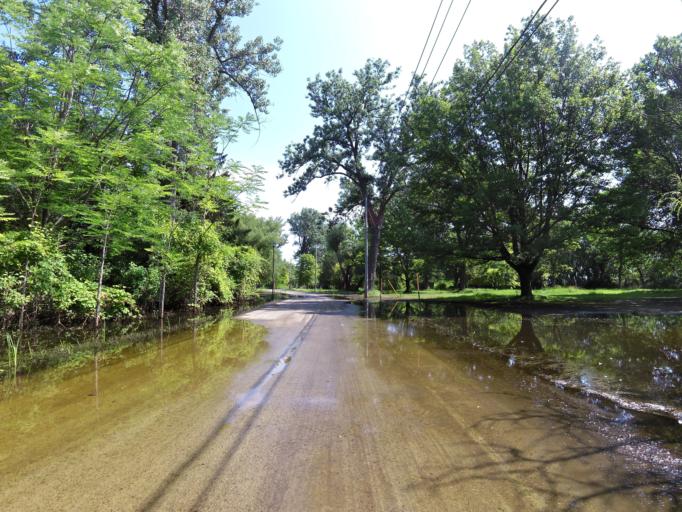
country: CA
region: Ontario
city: Toronto
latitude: 43.6224
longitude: -79.3636
